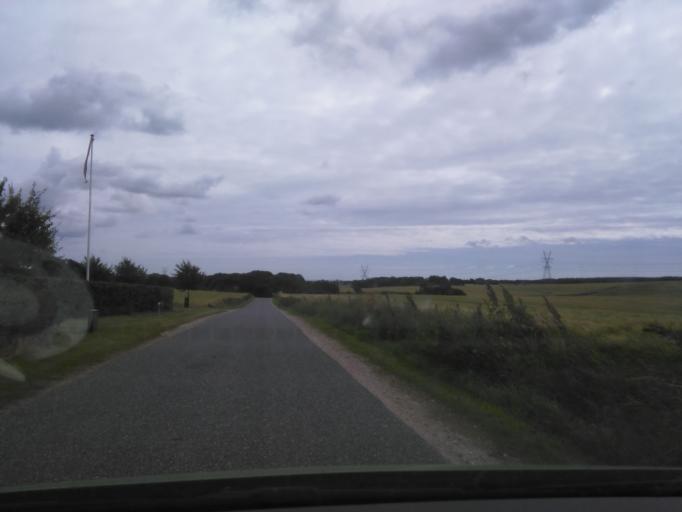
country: DK
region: Central Jutland
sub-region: Arhus Kommune
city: Solbjerg
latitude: 55.9852
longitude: 10.0753
